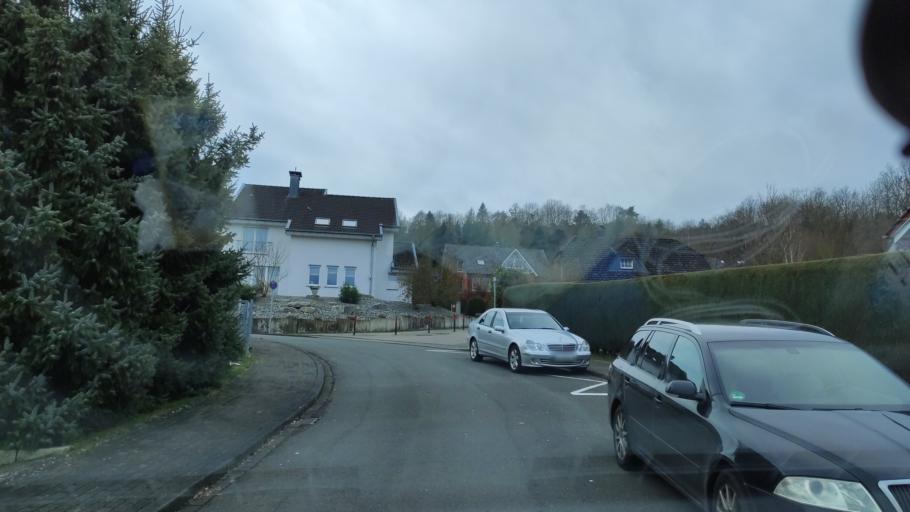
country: DE
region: North Rhine-Westphalia
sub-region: Regierungsbezirk Detmold
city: Hoexter
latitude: 51.7837
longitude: 9.3668
